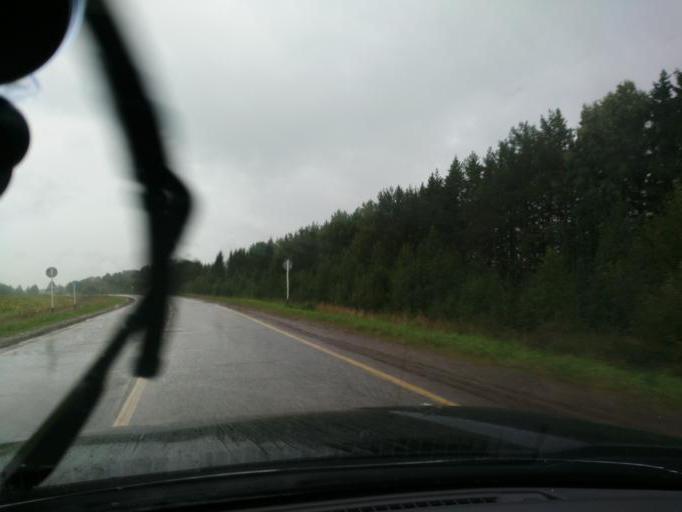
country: RU
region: Perm
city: Osa
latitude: 57.2895
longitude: 55.5940
